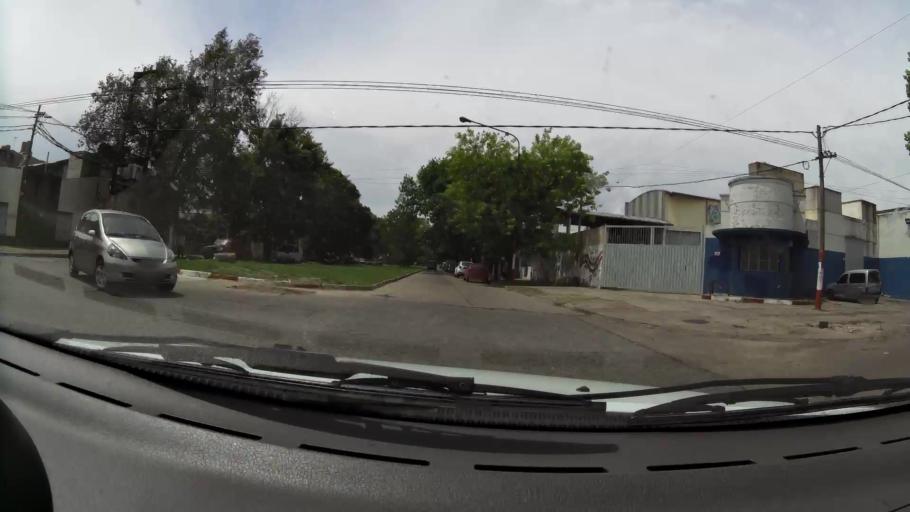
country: AR
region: Buenos Aires
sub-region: Partido de La Plata
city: La Plata
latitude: -34.9400
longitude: -57.9501
